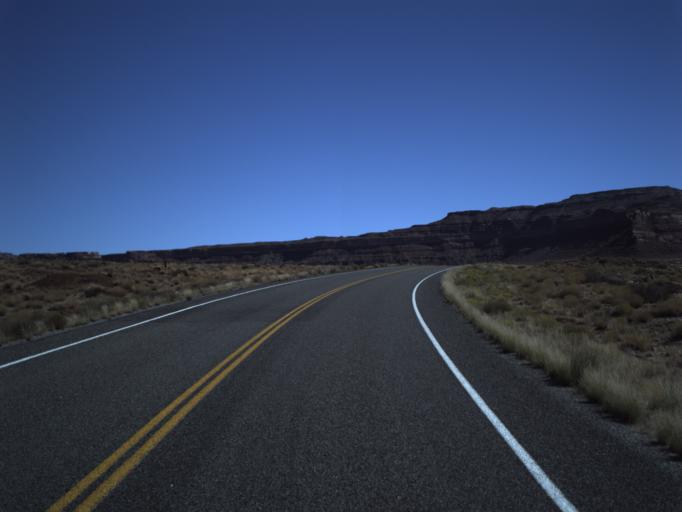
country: US
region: Utah
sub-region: San Juan County
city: Blanding
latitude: 37.9215
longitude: -110.3945
